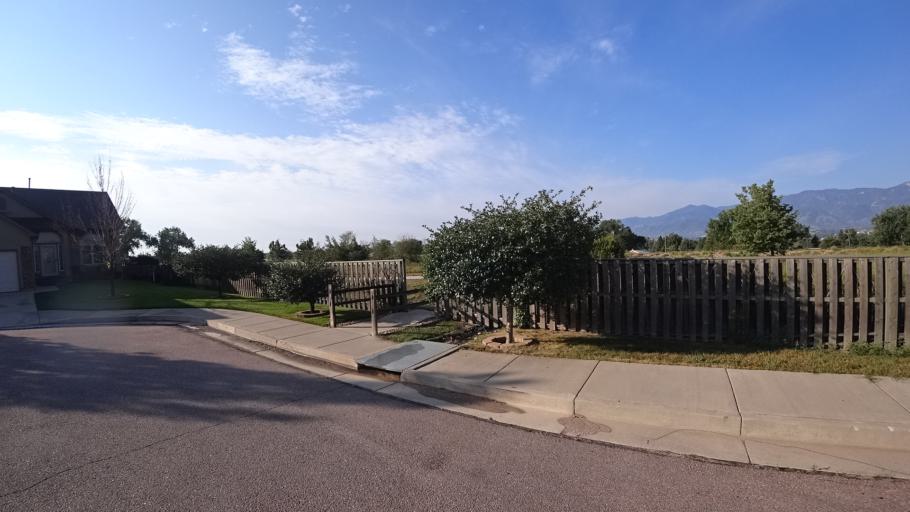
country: US
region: Colorado
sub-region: El Paso County
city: Colorado Springs
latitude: 38.8844
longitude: -104.8045
